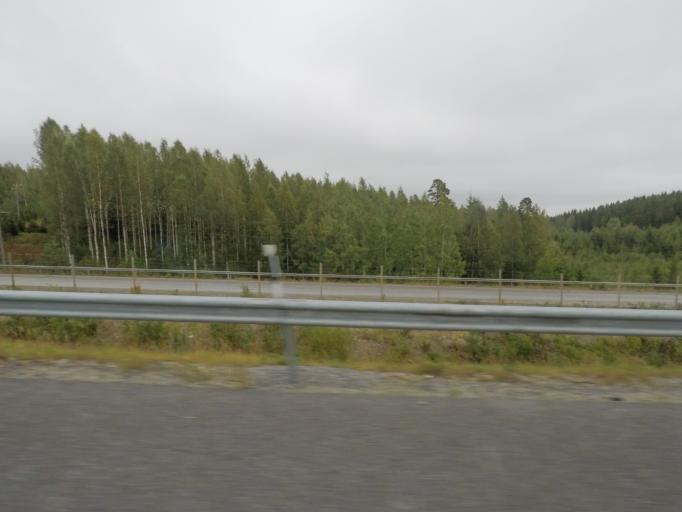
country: FI
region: Southern Savonia
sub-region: Mikkeli
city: Maentyharju
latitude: 61.4754
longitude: 26.7434
